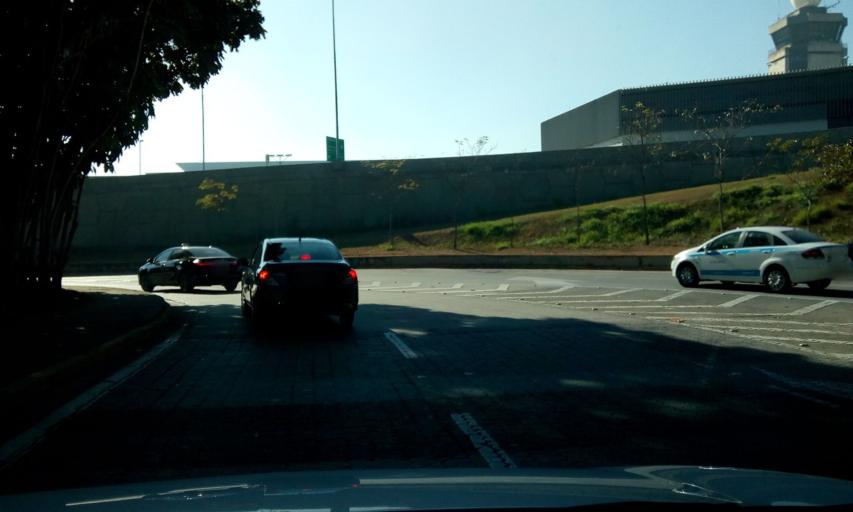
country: BR
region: Sao Paulo
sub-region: Guarulhos
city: Guarulhos
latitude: -23.4253
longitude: -46.4798
